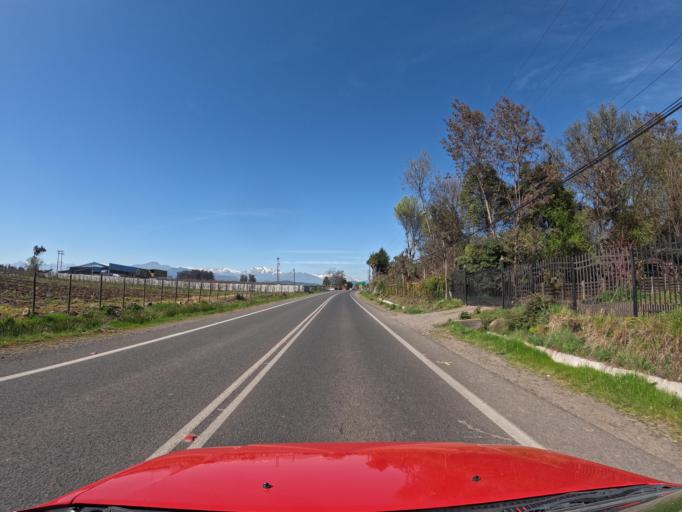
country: CL
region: Maule
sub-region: Provincia de Curico
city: Teno
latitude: -34.9656
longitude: -71.0393
